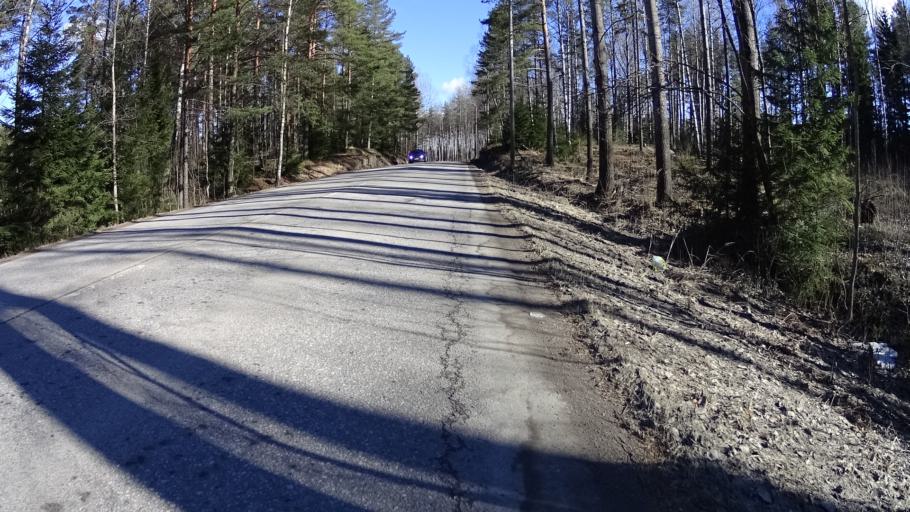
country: FI
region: Uusimaa
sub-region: Helsinki
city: Kauniainen
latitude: 60.2667
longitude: 24.7074
